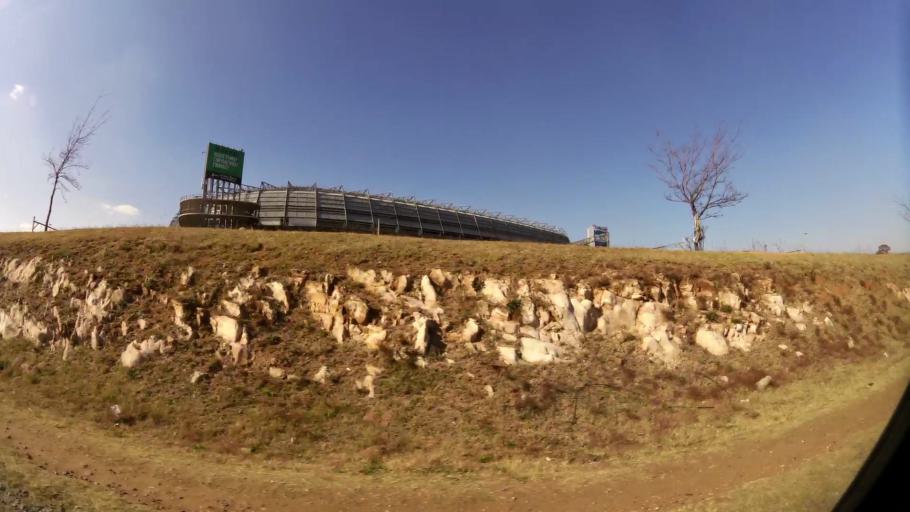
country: ZA
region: Gauteng
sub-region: City of Johannesburg Metropolitan Municipality
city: Soweto
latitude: -26.2304
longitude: 27.9210
